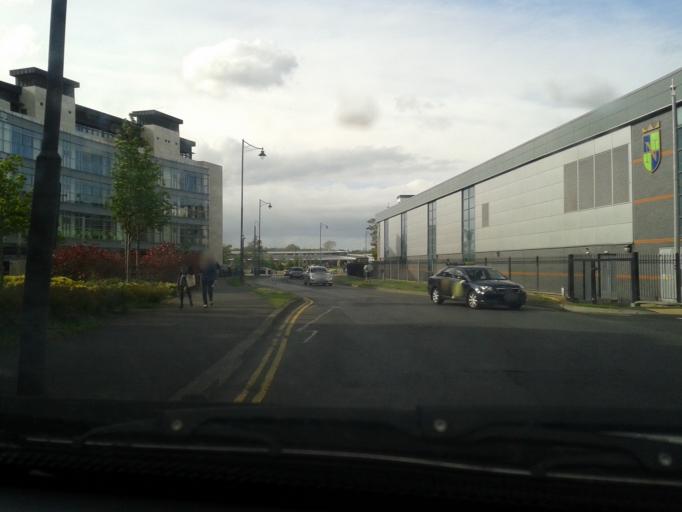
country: IE
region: Leinster
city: Ballymun
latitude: 53.4007
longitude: -6.2580
